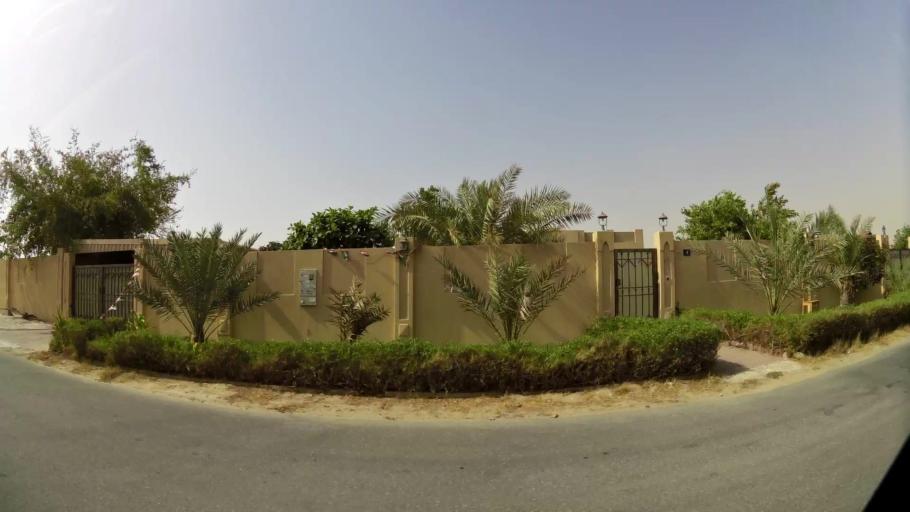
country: AE
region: Ash Shariqah
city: Sharjah
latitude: 25.2573
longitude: 55.4330
